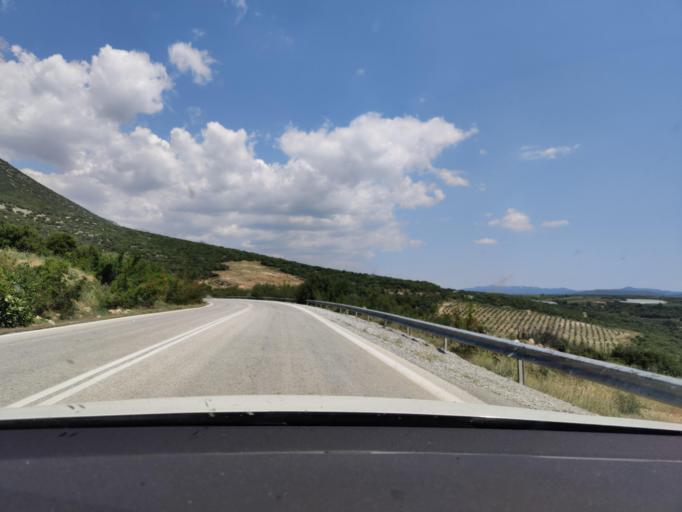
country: GR
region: East Macedonia and Thrace
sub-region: Nomos Kavalas
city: Paralia Ofryniou
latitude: 40.8056
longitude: 23.9700
